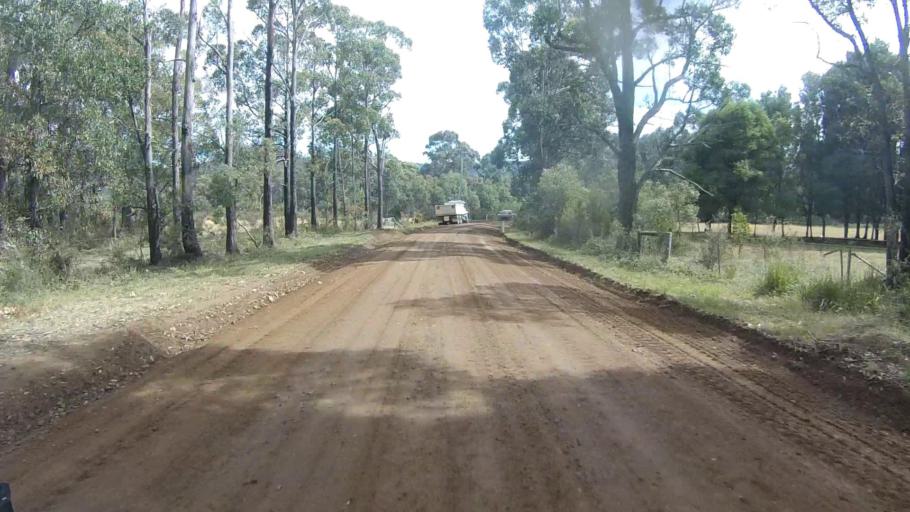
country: AU
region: Tasmania
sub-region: Sorell
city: Sorell
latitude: -42.7767
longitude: 147.8088
